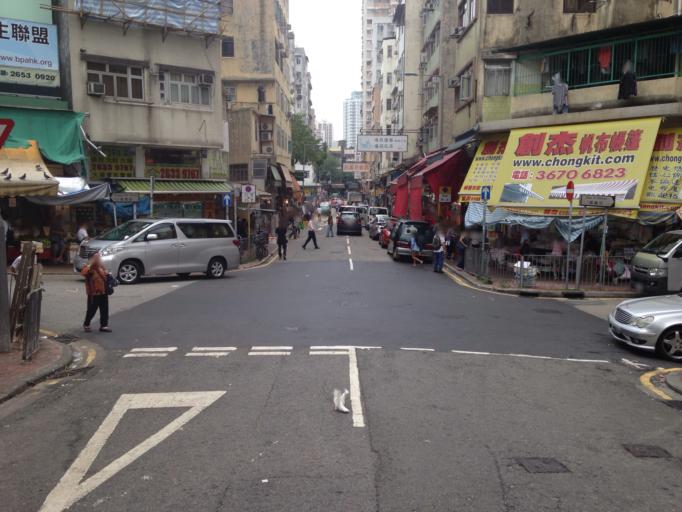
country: HK
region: Tai Po
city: Tai Po
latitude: 22.4479
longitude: 114.1651
